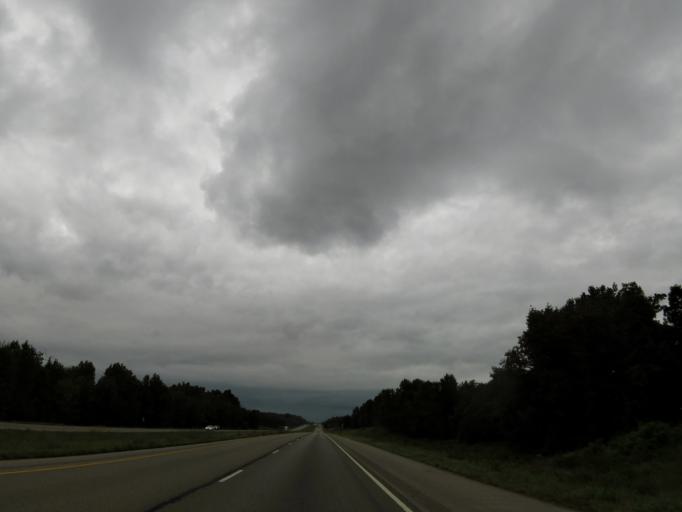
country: US
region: Illinois
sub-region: Massac County
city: Metropolis
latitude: 37.2075
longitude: -88.6950
